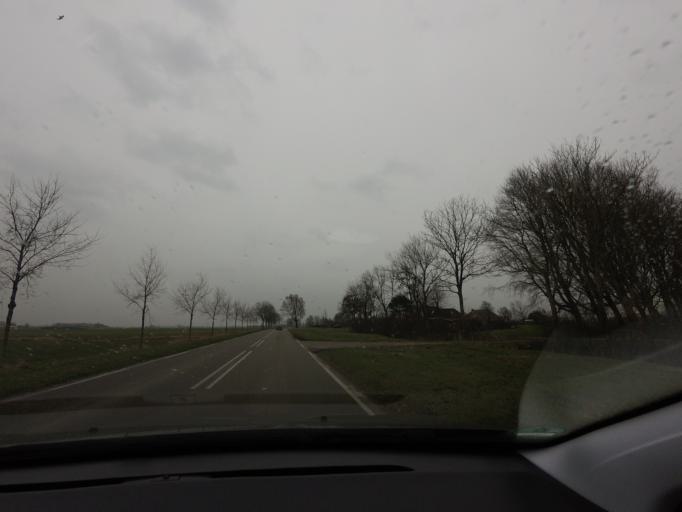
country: NL
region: Friesland
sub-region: Gemeente Franekeradeel
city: Franeker
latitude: 53.1798
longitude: 5.5566
